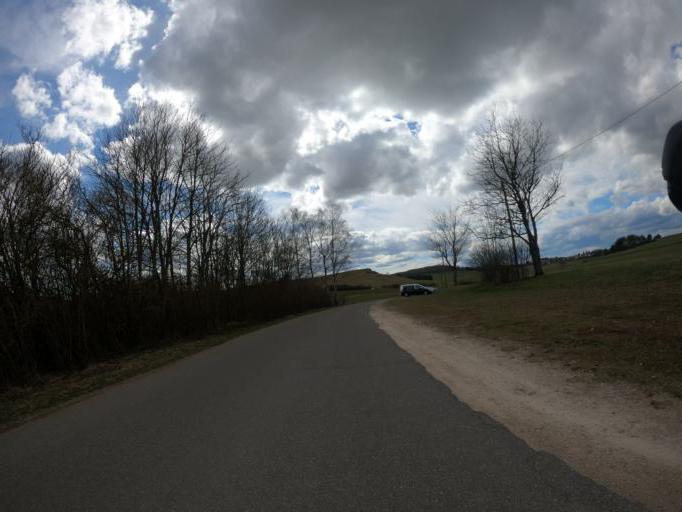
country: DE
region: Baden-Wuerttemberg
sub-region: Tuebingen Region
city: Pfullingen
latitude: 48.3876
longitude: 9.2111
